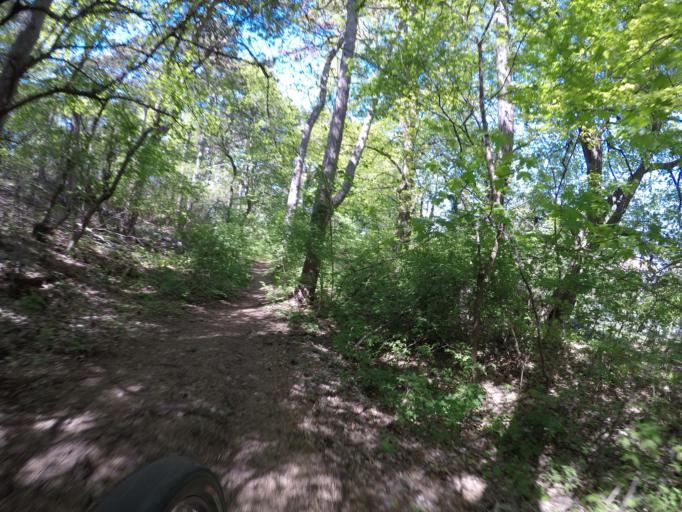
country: AT
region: Lower Austria
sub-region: Politischer Bezirk Modling
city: Modling
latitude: 48.0686
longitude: 16.2814
